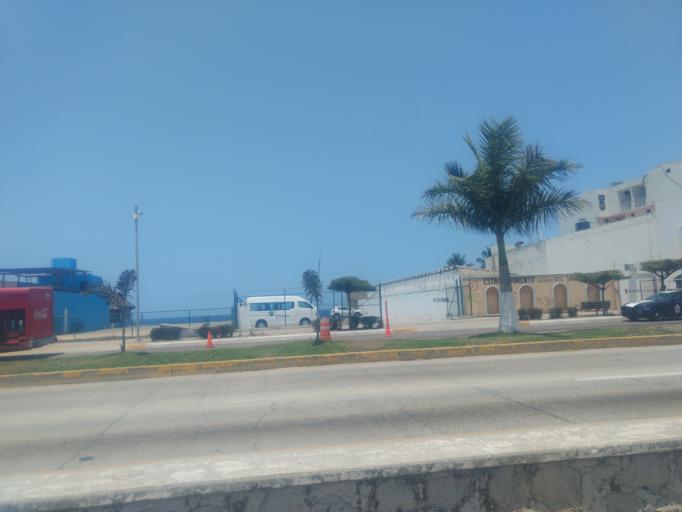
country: MX
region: Colima
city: Tapeixtles
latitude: 19.0893
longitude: -104.3127
